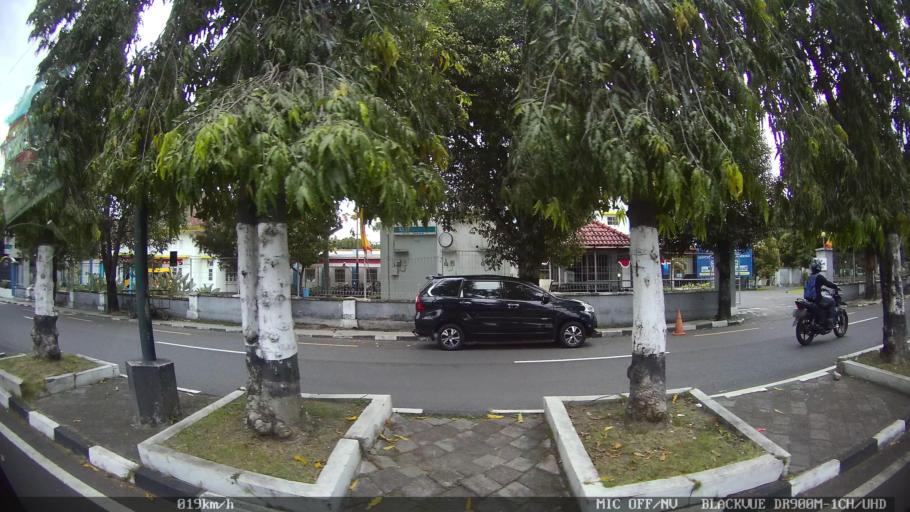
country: ID
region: Daerah Istimewa Yogyakarta
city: Yogyakarta
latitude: -7.7949
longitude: 110.3833
